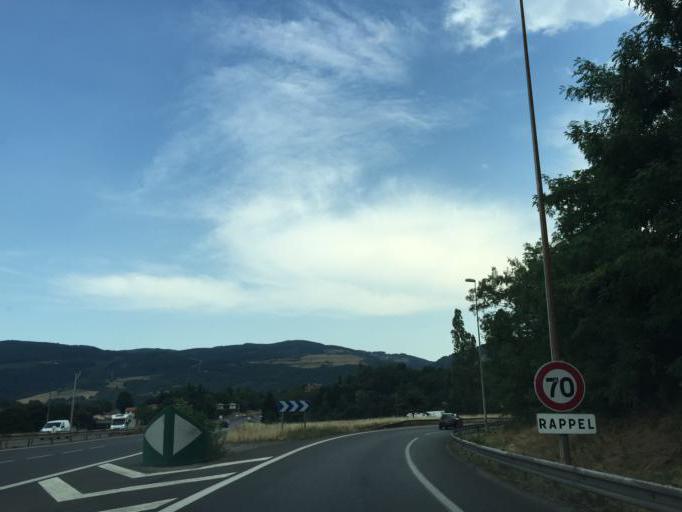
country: FR
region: Rhone-Alpes
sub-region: Departement de la Loire
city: Saint-Jean-Bonnefonds
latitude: 45.4430
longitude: 4.4296
